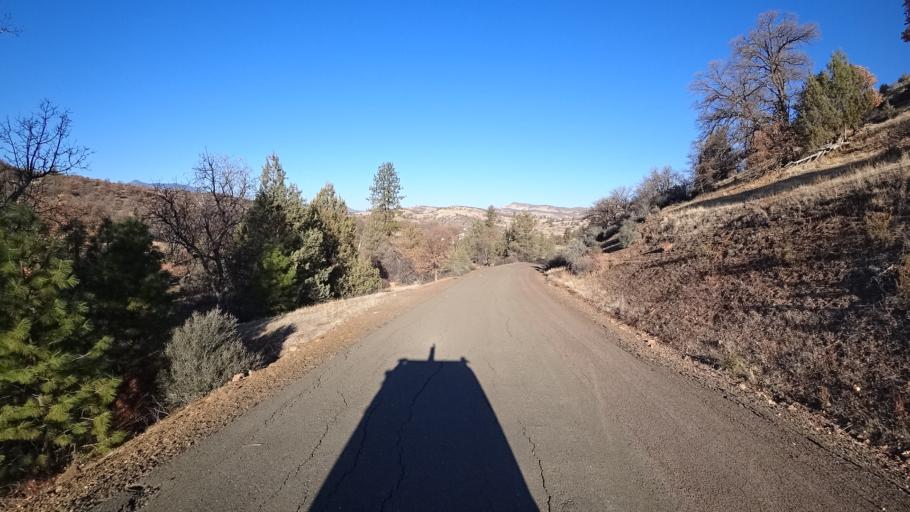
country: US
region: California
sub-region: Siskiyou County
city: Montague
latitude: 41.8934
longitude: -122.4997
